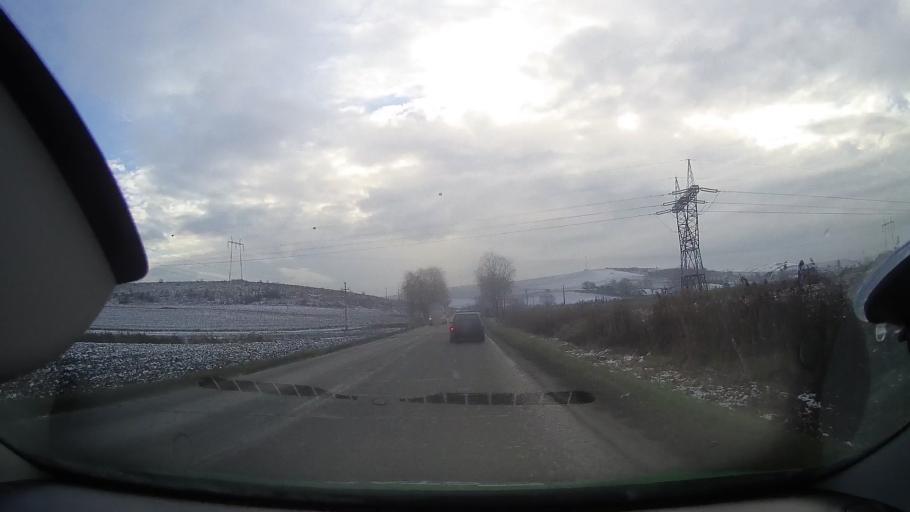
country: RO
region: Mures
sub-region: Comuna Cucerdea
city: Cucerdea
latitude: 46.4223
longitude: 24.2594
